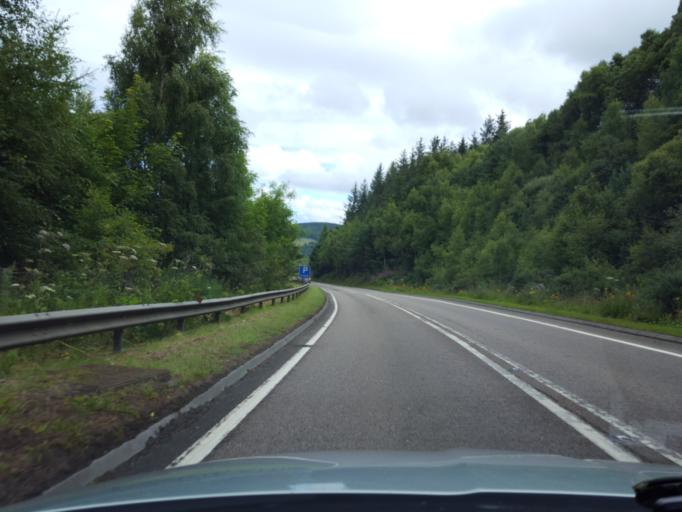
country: GB
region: Scotland
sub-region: Moray
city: Rothes
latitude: 57.4841
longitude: -3.1945
